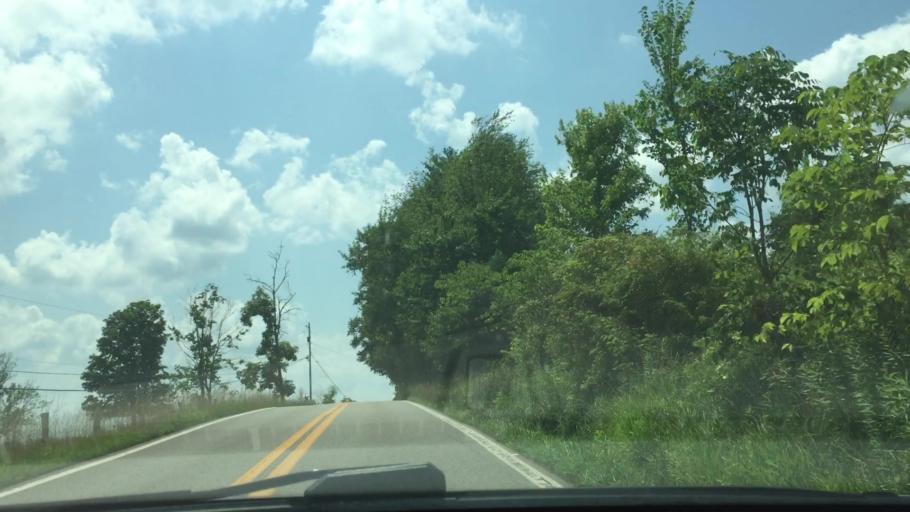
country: US
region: West Virginia
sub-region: Wetzel County
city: New Martinsville
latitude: 39.7009
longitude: -80.7555
